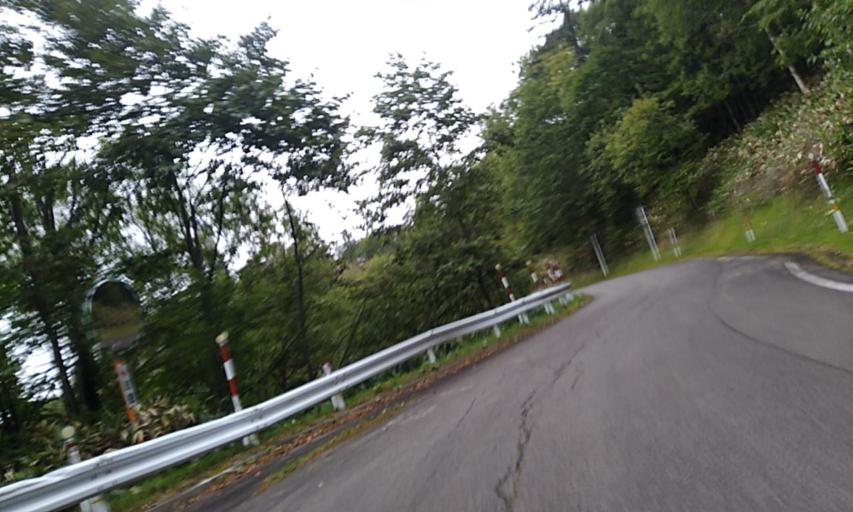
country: JP
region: Hokkaido
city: Bihoro
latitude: 43.5674
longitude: 144.2026
